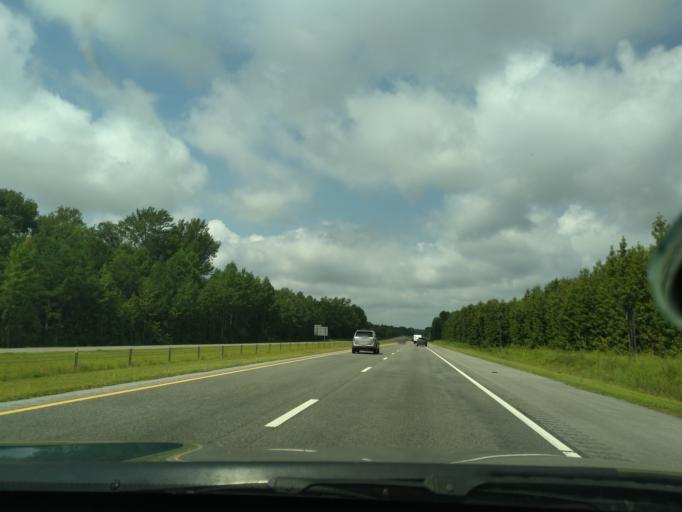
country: US
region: North Carolina
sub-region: Martin County
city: Robersonville
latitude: 35.8334
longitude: -77.2744
